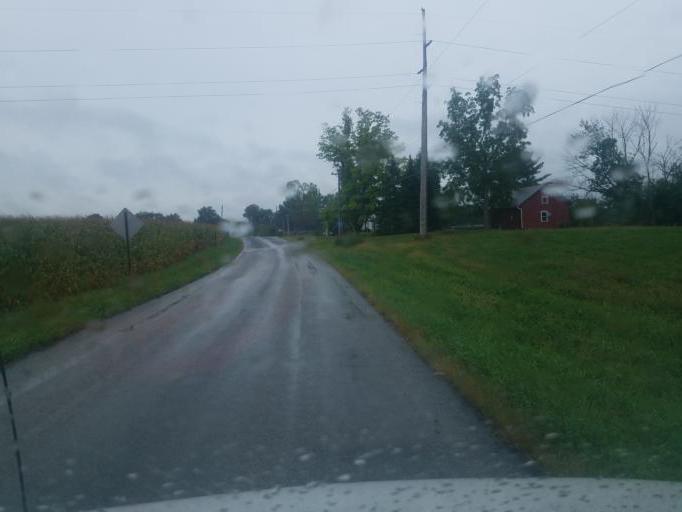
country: US
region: Ohio
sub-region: Wayne County
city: Rittman
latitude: 40.9878
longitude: -81.8156
